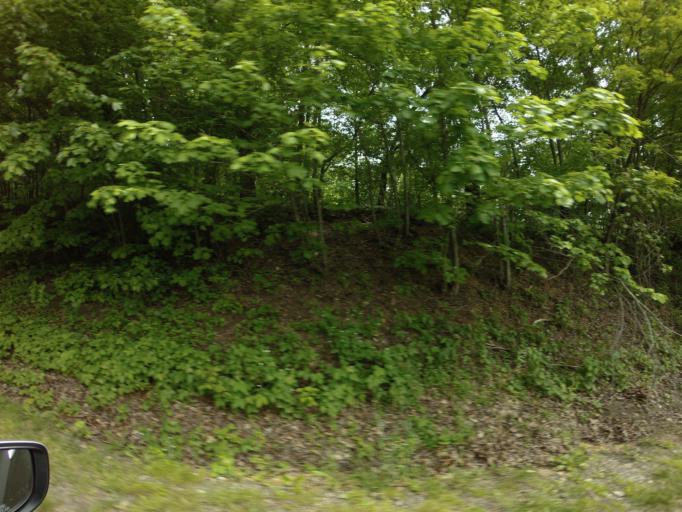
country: US
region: Maryland
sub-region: Carroll County
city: New Windsor
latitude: 39.4927
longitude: -77.1430
